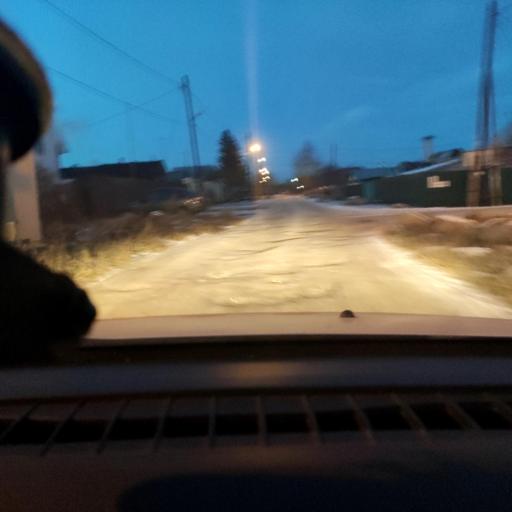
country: RU
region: Samara
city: Smyshlyayevka
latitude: 53.2545
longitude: 50.3553
